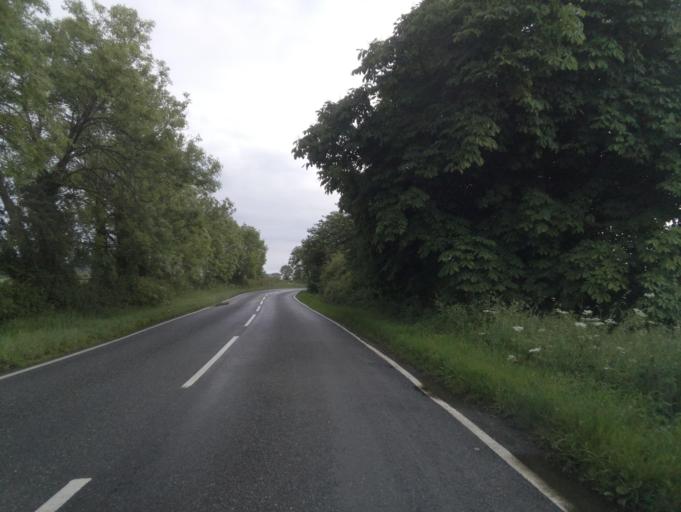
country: GB
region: England
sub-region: Lincolnshire
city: Great Gonerby
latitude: 53.0194
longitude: -0.6581
